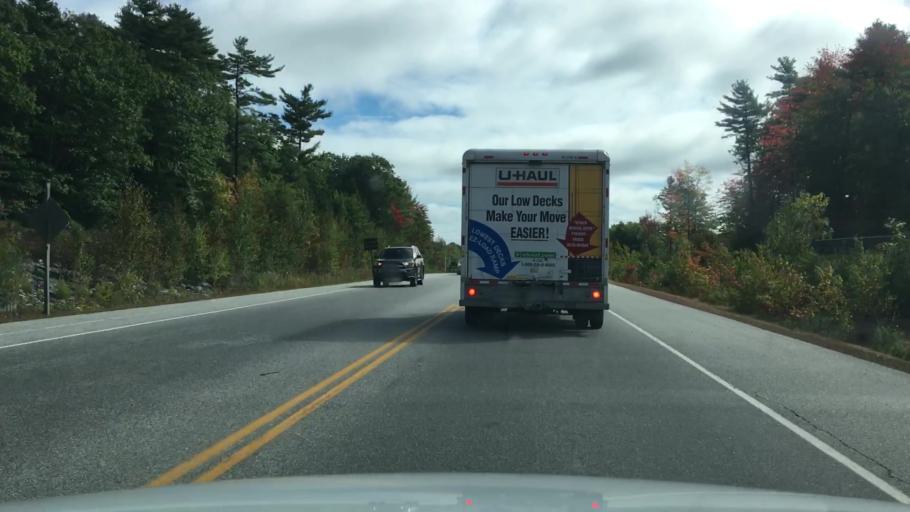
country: US
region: Maine
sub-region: Sagadahoc County
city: Topsham
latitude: 43.9369
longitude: -69.9600
